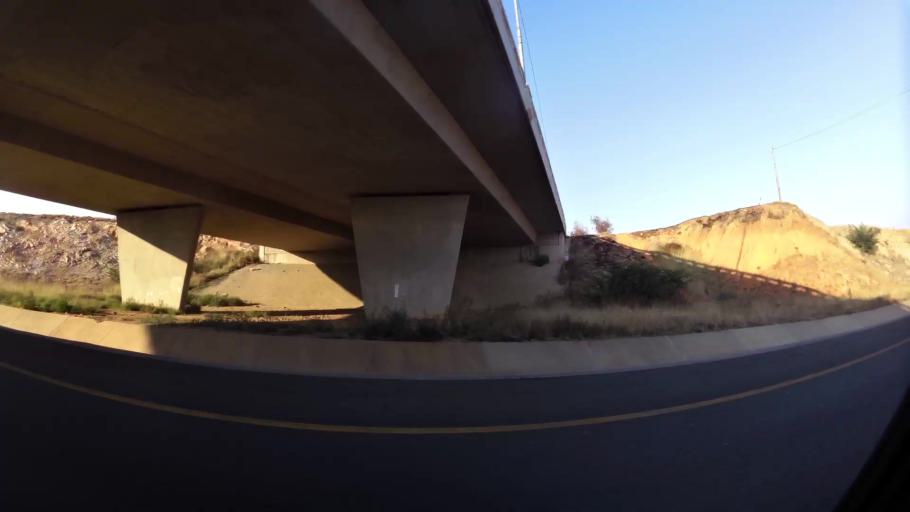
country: ZA
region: Gauteng
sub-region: City of Johannesburg Metropolitan Municipality
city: Roodepoort
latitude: -26.2194
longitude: 27.9394
